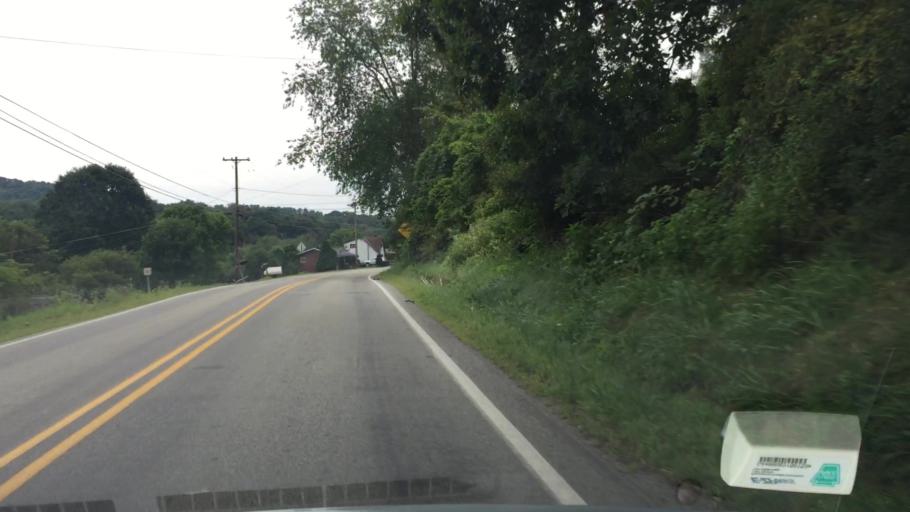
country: US
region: Pennsylvania
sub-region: Allegheny County
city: Curtisville
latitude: 40.6804
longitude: -79.8309
